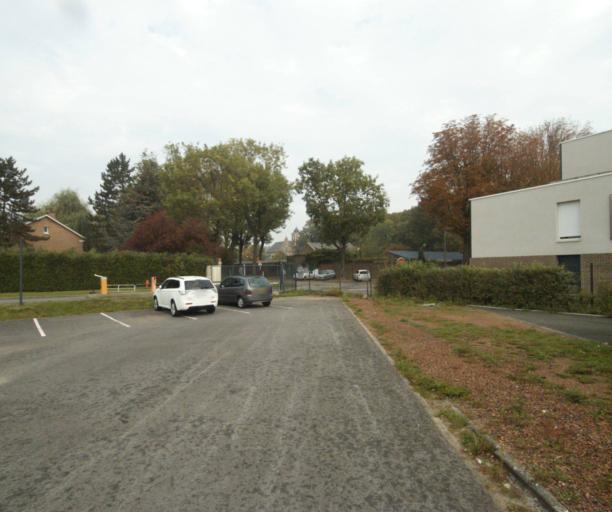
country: FR
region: Nord-Pas-de-Calais
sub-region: Departement du Nord
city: Seclin
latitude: 50.5466
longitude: 3.0204
